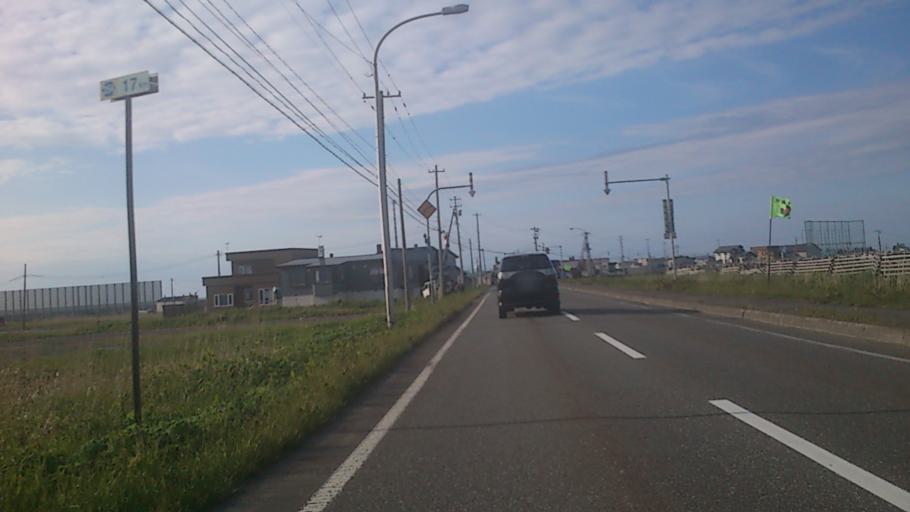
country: JP
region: Hokkaido
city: Wakkanai
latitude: 45.4428
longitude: 141.6456
